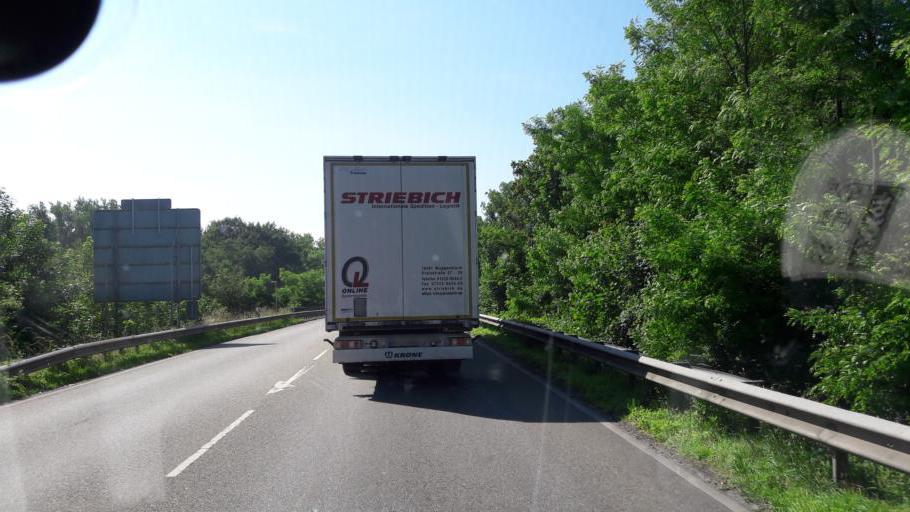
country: DE
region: Baden-Wuerttemberg
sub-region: Karlsruhe Region
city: Otigheim
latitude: 48.8683
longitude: 8.2349
